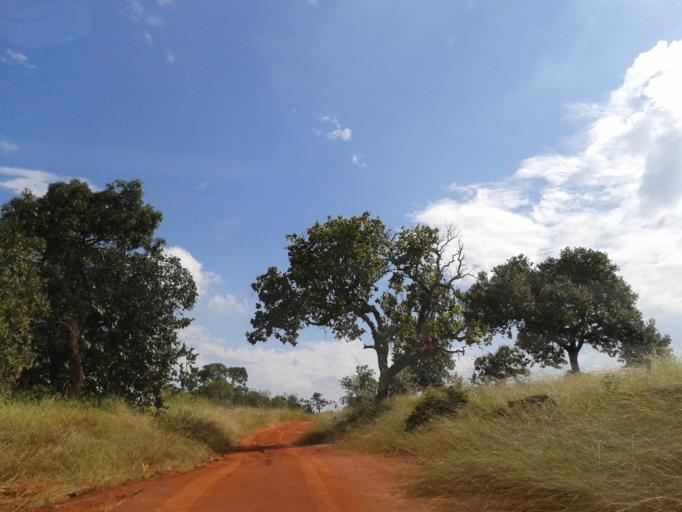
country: BR
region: Minas Gerais
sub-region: Campina Verde
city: Campina Verde
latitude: -19.3922
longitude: -49.6546
